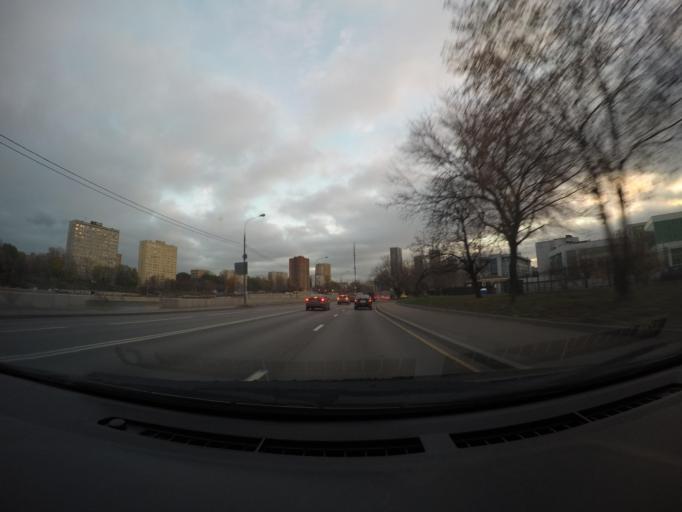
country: RU
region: Moscow
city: Taganskiy
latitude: 55.7251
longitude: 37.6560
